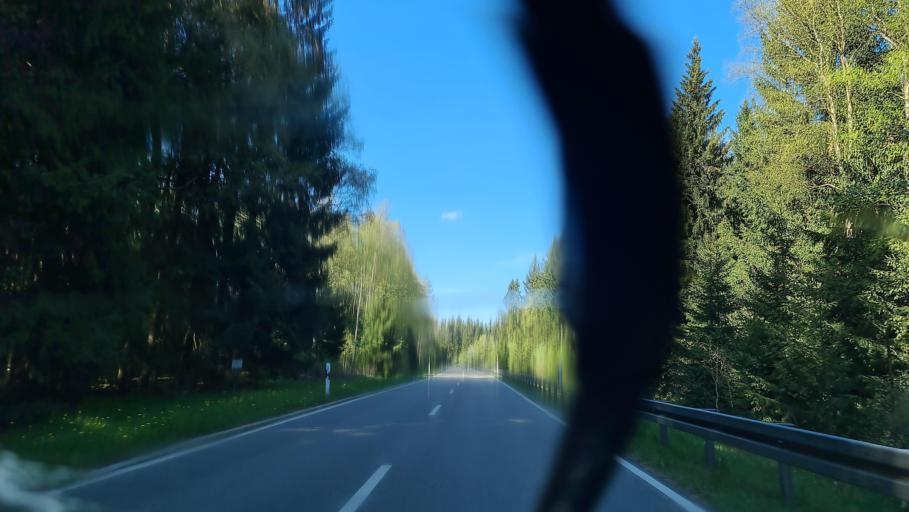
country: DE
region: Saxony
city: Hammerbrucke
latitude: 50.4261
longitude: 12.3994
